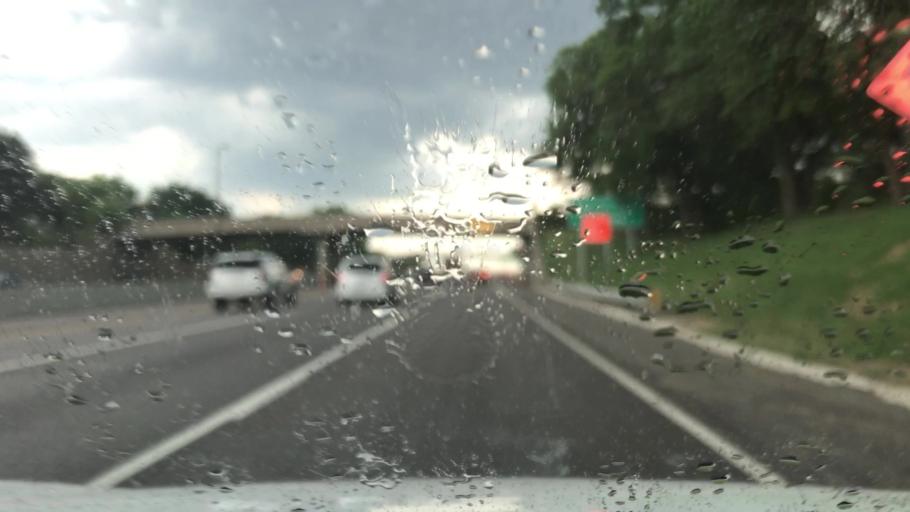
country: US
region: Missouri
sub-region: Saint Louis County
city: Richmond Heights
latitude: 38.6190
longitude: -90.2762
